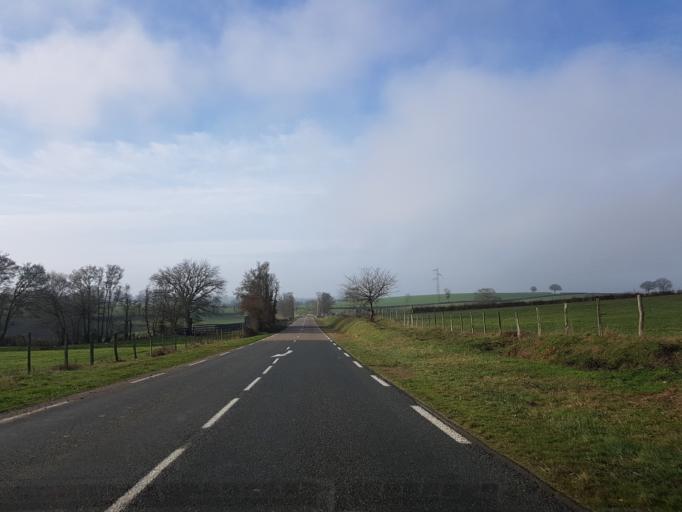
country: FR
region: Bourgogne
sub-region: Departement de Saone-et-Loire
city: Gueugnon
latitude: 46.5980
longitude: 3.9911
